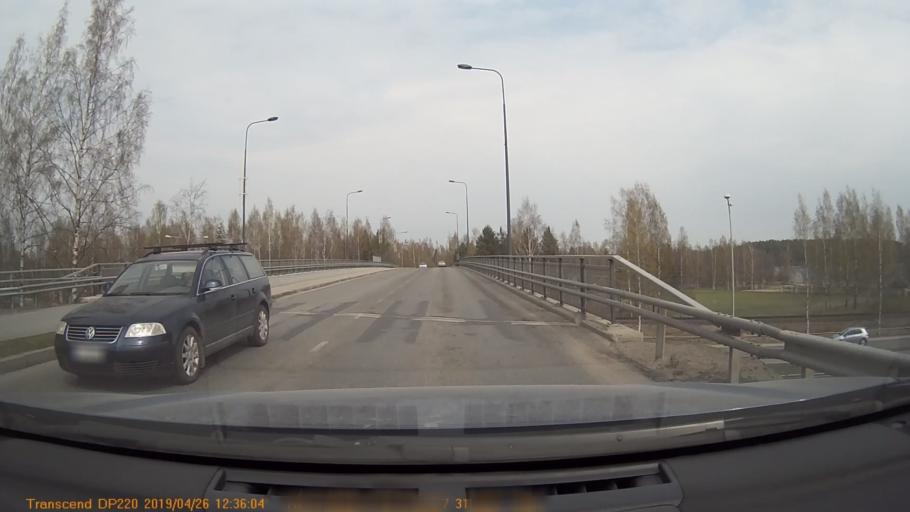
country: FI
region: Pirkanmaa
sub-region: Tampere
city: Yloejaervi
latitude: 61.5502
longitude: 23.5974
